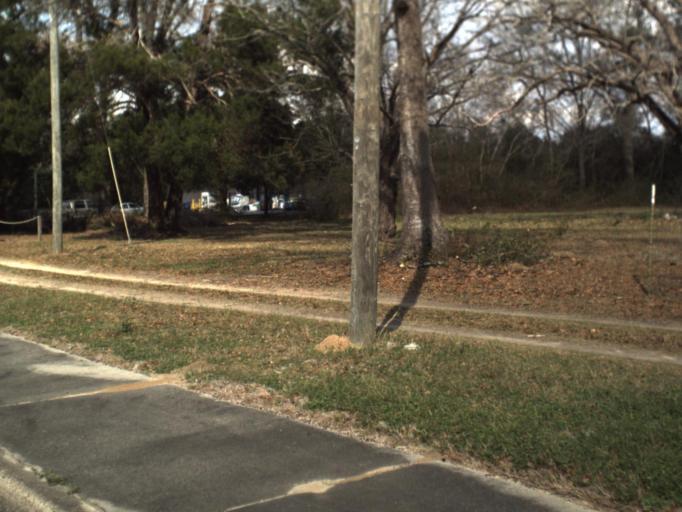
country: US
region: Florida
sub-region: Bay County
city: Youngstown
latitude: 30.3755
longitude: -85.4383
